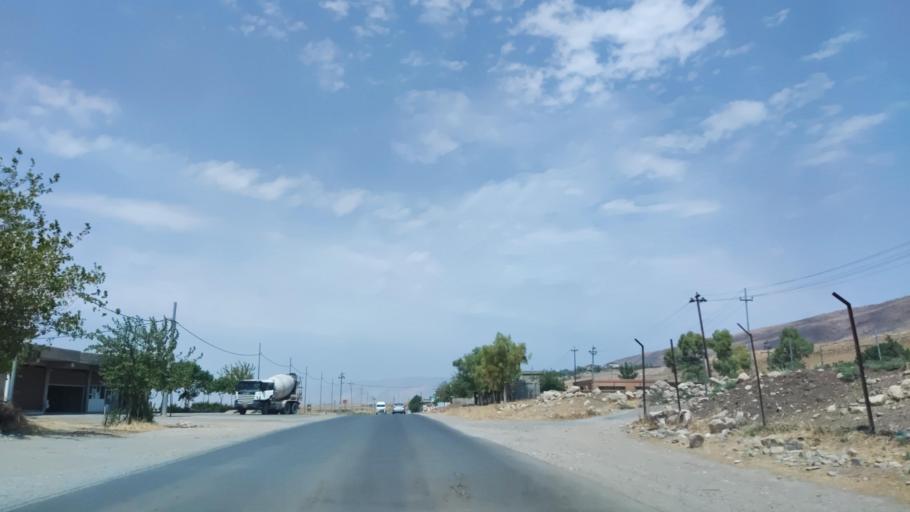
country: IQ
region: Arbil
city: Shaqlawah
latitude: 36.5285
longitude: 44.3600
